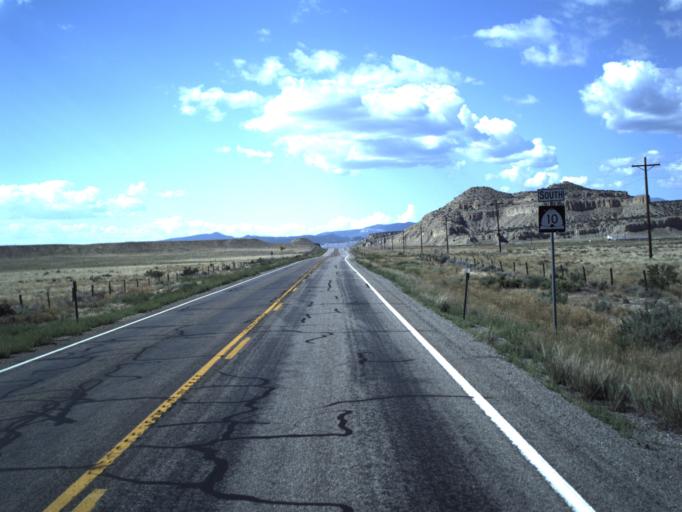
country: US
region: Utah
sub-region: Emery County
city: Ferron
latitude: 38.8584
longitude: -111.3030
